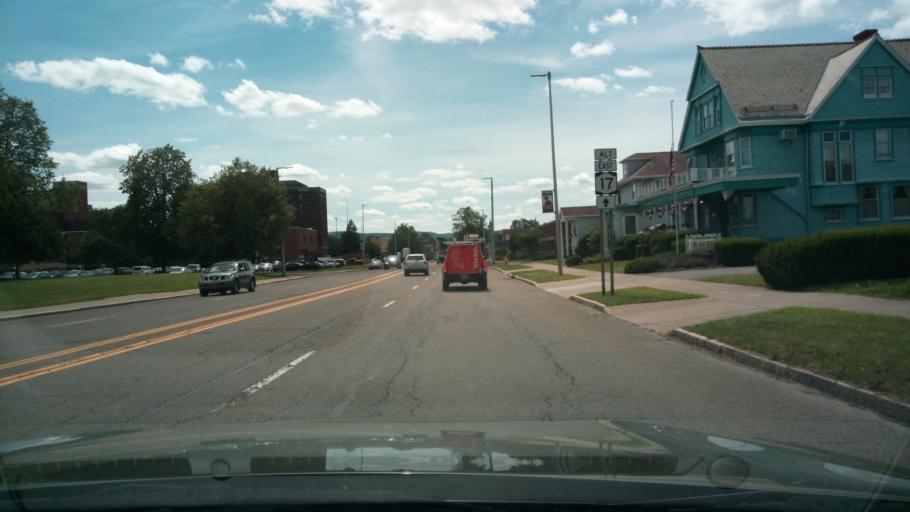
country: US
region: New York
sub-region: Chemung County
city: Elmira
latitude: 42.0936
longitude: -76.7956
